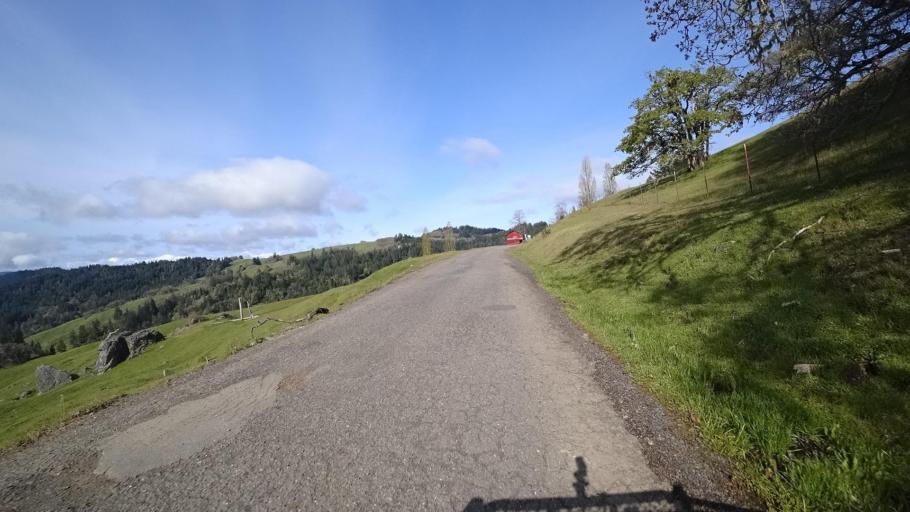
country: US
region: California
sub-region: Humboldt County
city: Hydesville
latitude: 40.6421
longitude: -123.9129
